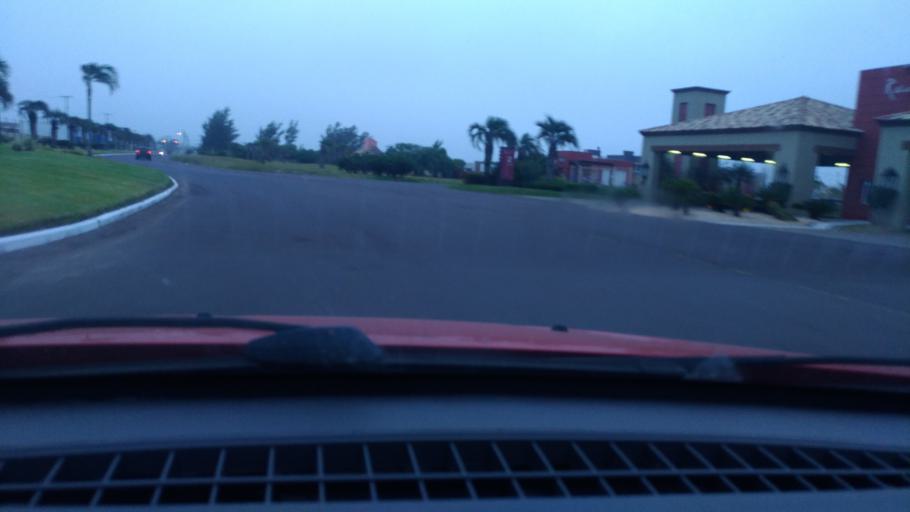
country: BR
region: Rio Grande do Sul
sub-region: Capao Da Canoa
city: Capao da Canoa
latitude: -29.8495
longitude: -50.0759
